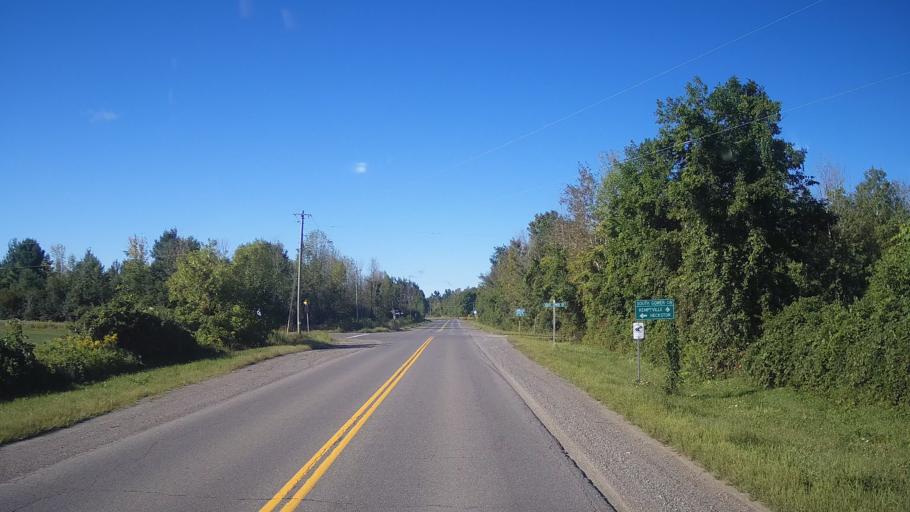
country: CA
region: Ontario
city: Bells Corners
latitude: 45.0896
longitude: -75.6283
